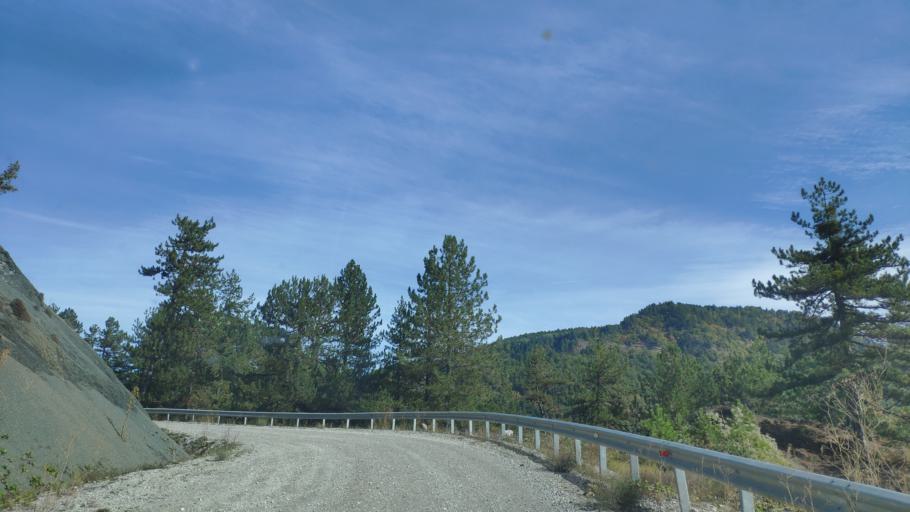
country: AL
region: Korce
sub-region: Rrethi i Devollit
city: Miras
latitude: 40.4181
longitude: 20.8701
